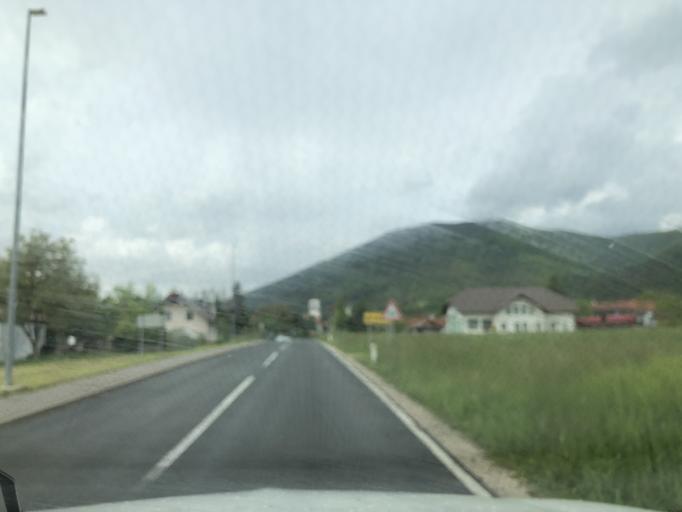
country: SI
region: Cerknica
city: Cerknica
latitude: 45.7682
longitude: 14.4268
